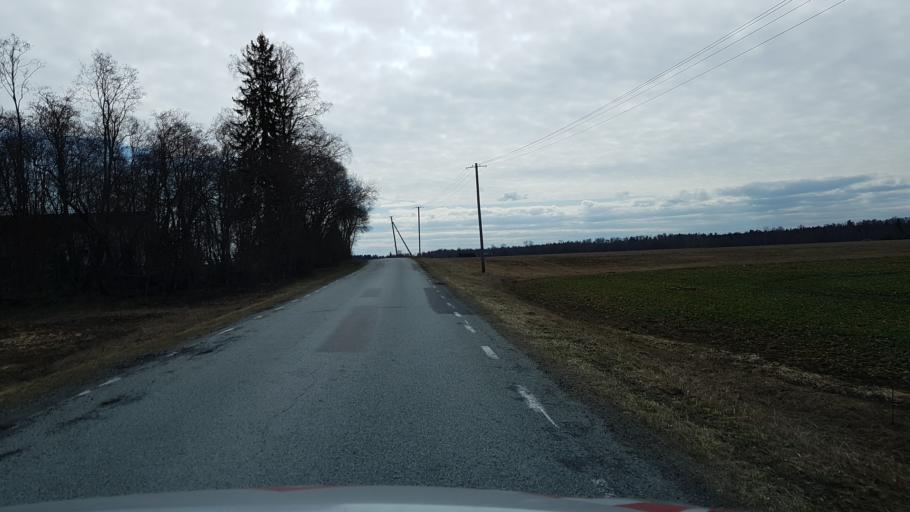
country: EE
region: Laeaene-Virumaa
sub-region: Haljala vald
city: Haljala
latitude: 59.4143
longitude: 26.2513
